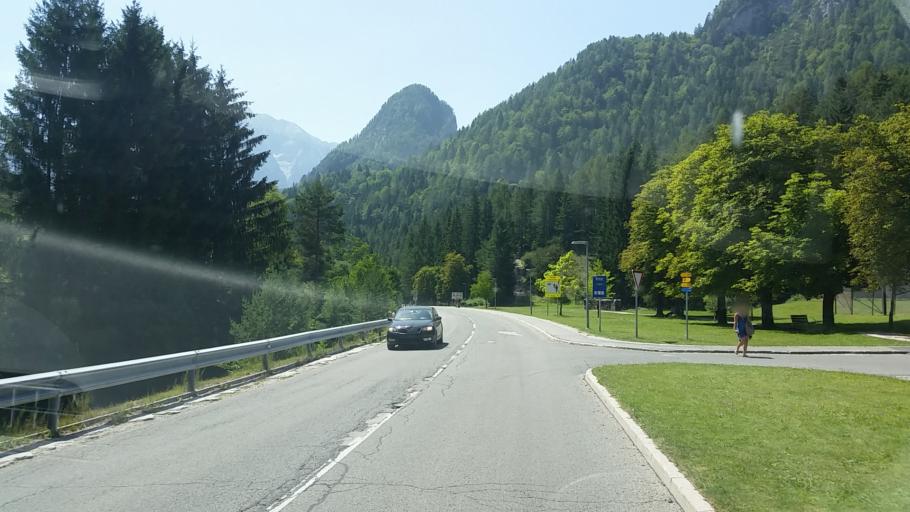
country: SI
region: Kranjska Gora
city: Kranjska Gora
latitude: 46.4808
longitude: 13.7814
